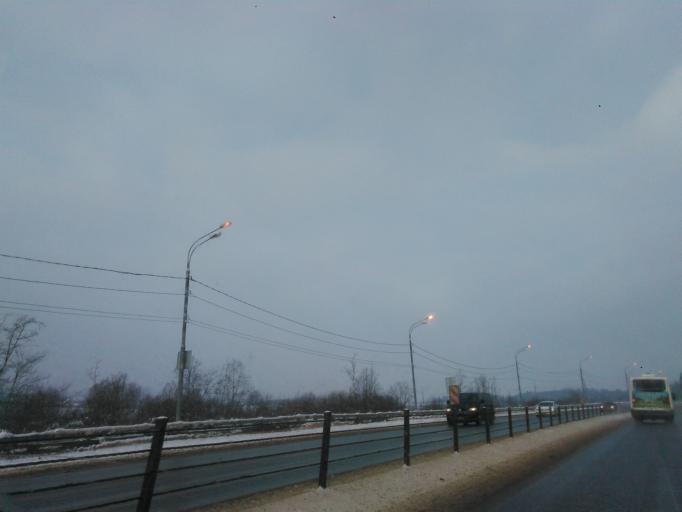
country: RU
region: Moskovskaya
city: Dedenevo
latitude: 56.2168
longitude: 37.5216
